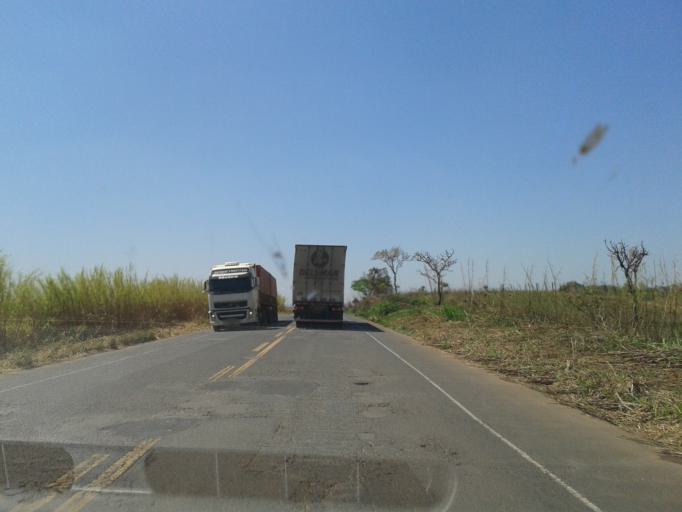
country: BR
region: Minas Gerais
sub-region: Araxa
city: Araxa
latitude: -19.4294
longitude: -47.2297
